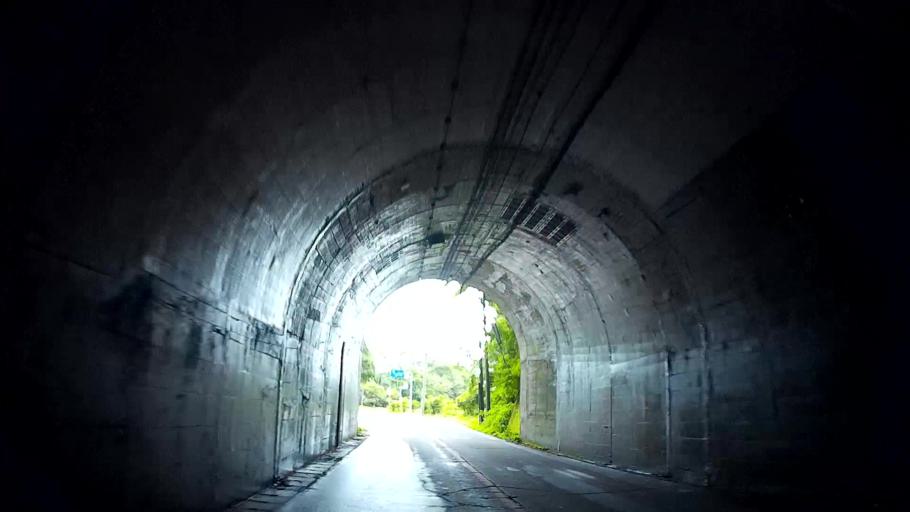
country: JP
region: Oita
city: Hita
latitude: 33.1382
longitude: 130.9712
